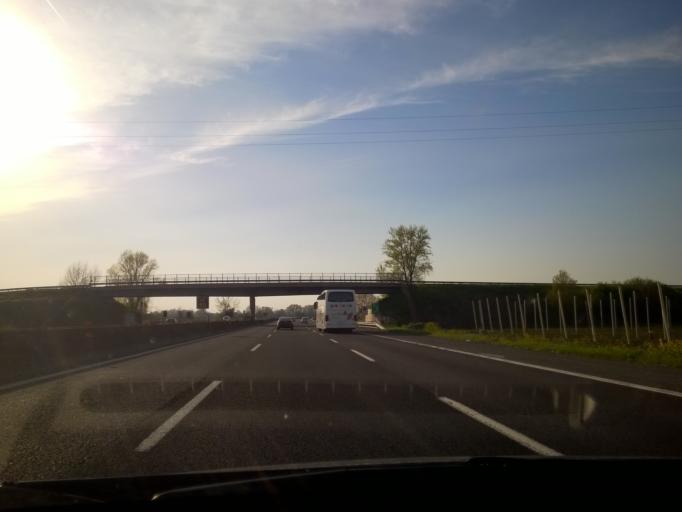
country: IT
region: Emilia-Romagna
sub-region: Provincia di Bologna
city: Mordano
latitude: 44.3607
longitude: 11.7939
